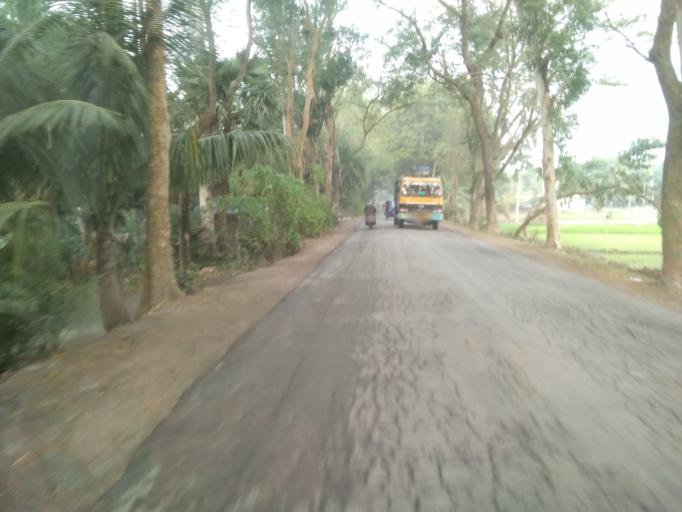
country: BD
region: Khulna
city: Satkhira
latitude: 22.6755
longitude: 89.0160
